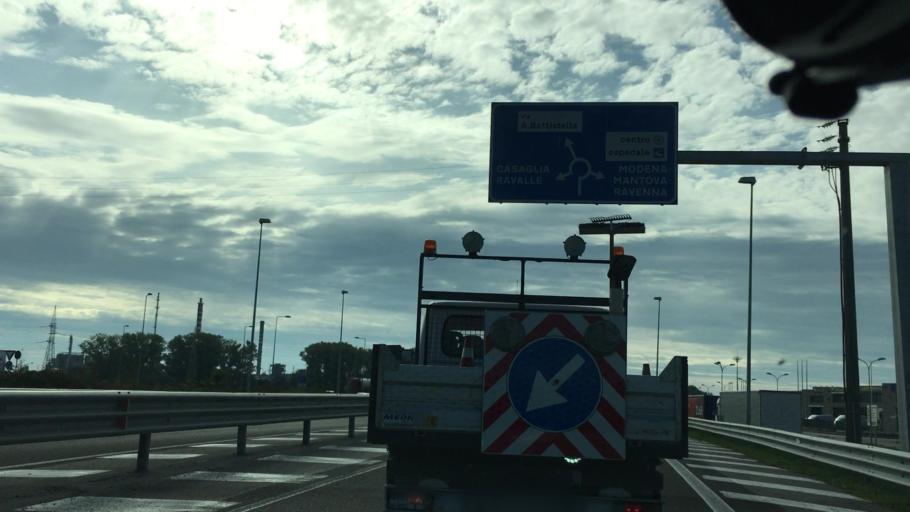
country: IT
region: Emilia-Romagna
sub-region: Provincia di Ferrara
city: Porotto-Cassama
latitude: 44.8664
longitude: 11.5740
